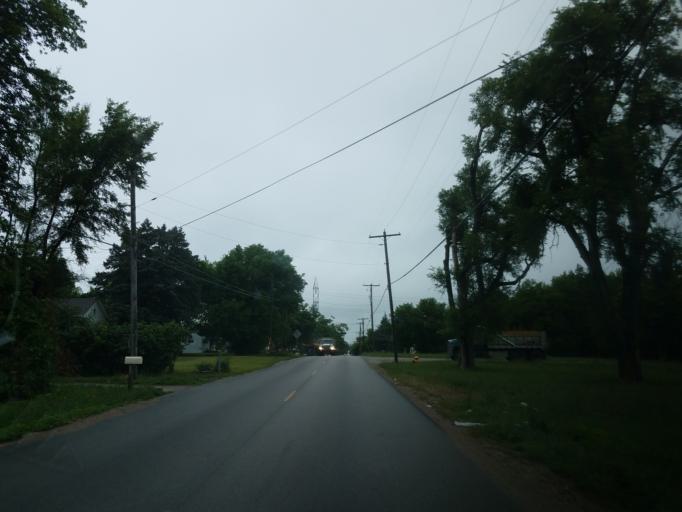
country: US
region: Illinois
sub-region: McLean County
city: Bloomington
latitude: 40.4602
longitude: -88.9816
